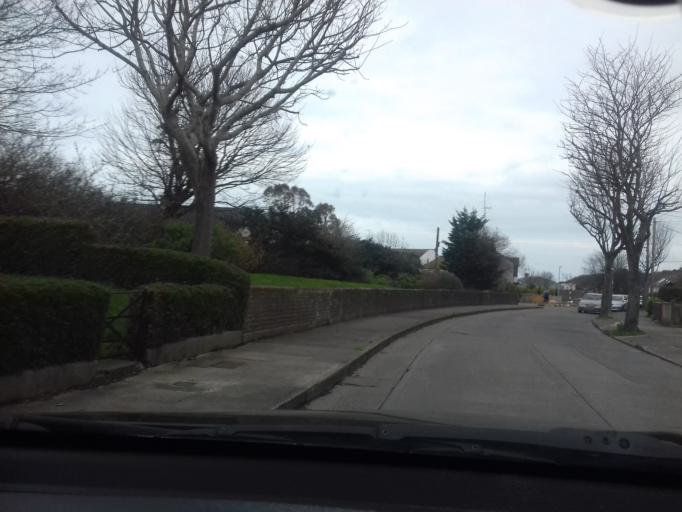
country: IE
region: Leinster
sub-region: Fingal County
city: Howth
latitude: 53.3858
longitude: -6.0689
